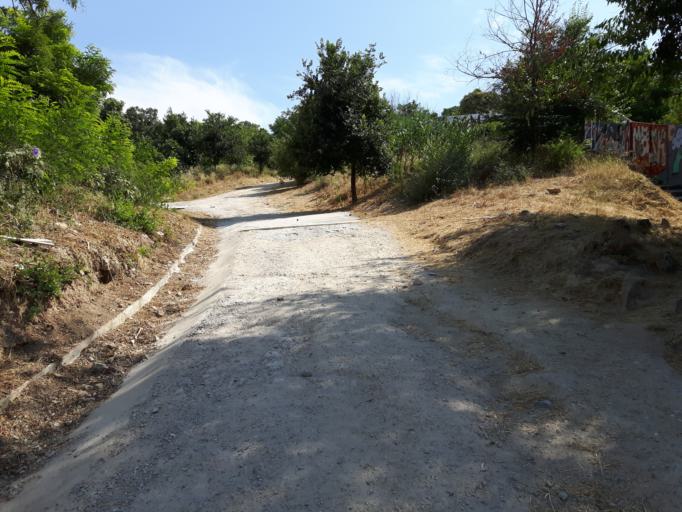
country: ES
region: Catalonia
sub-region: Provincia de Barcelona
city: Sants-Montjuic
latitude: 41.3703
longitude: 2.1633
